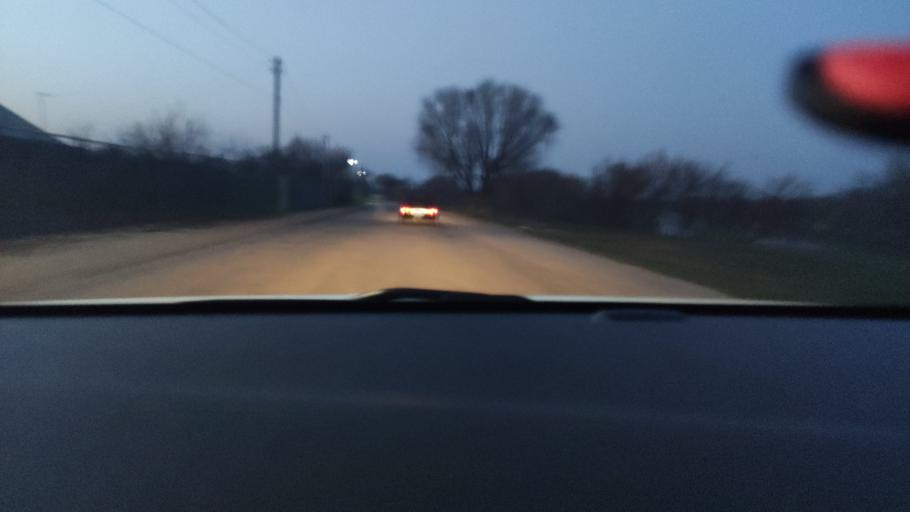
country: RU
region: Voronezj
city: Shilovo
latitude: 51.4745
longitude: 39.0225
